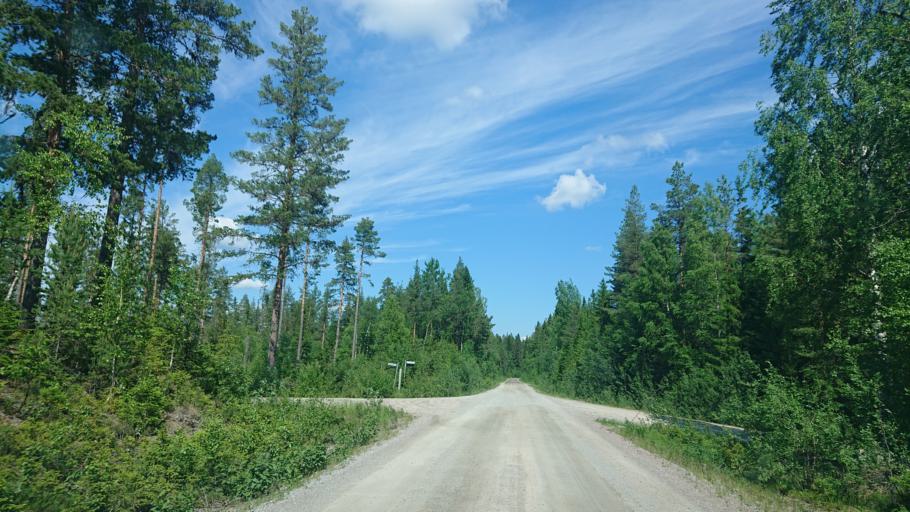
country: SE
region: Vaesternorrland
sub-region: Solleftea Kommun
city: Solleftea
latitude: 62.9564
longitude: 17.1449
